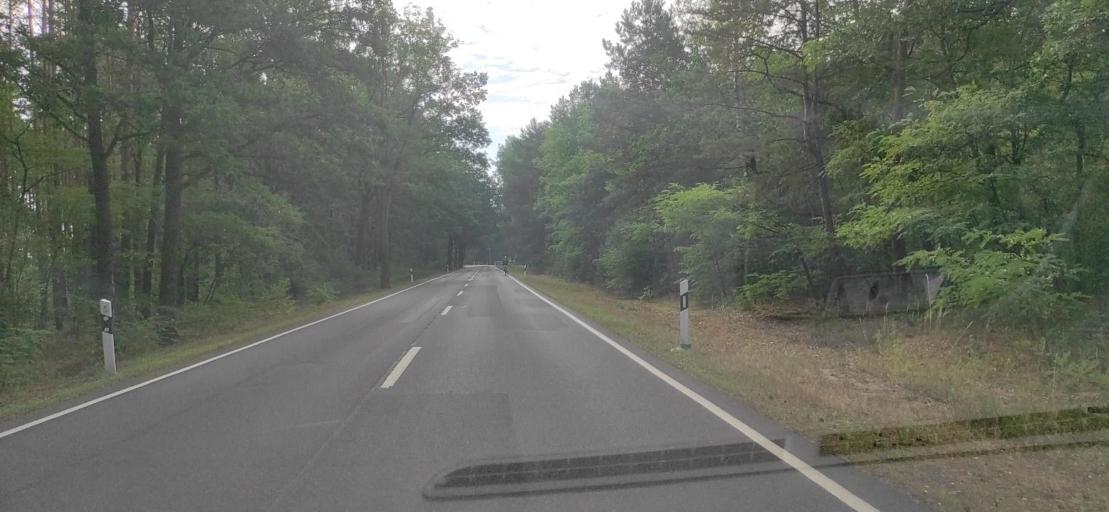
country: DE
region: Brandenburg
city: Forst
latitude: 51.7091
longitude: 14.6755
